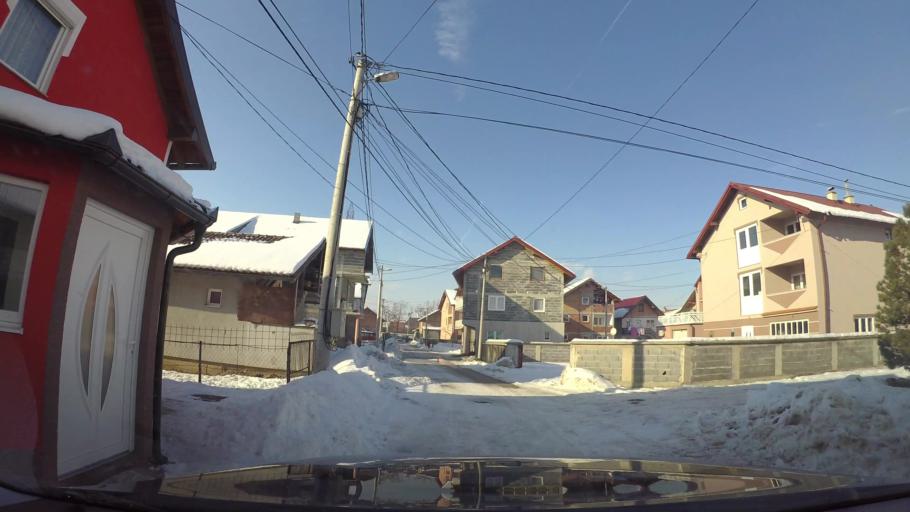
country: BA
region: Federation of Bosnia and Herzegovina
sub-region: Kanton Sarajevo
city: Sarajevo
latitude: 43.8062
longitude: 18.3313
